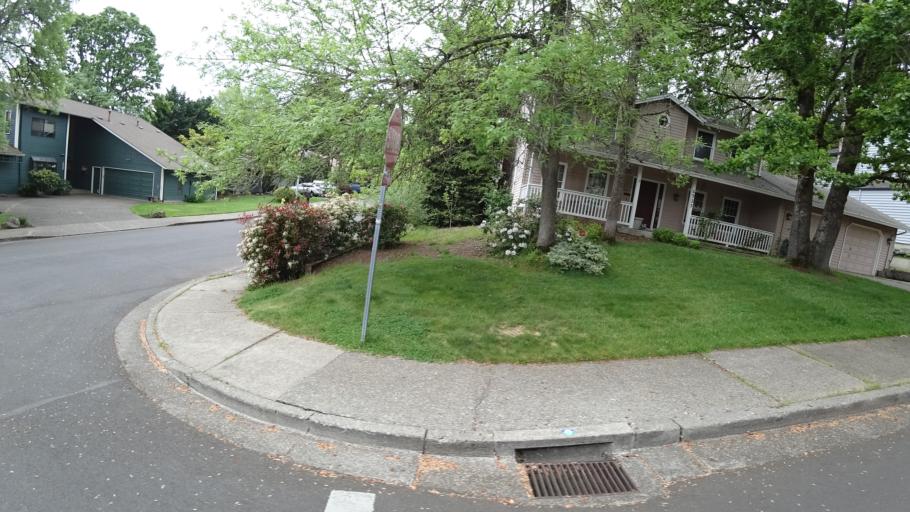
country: US
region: Oregon
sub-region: Washington County
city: Aloha
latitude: 45.4696
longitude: -122.8419
